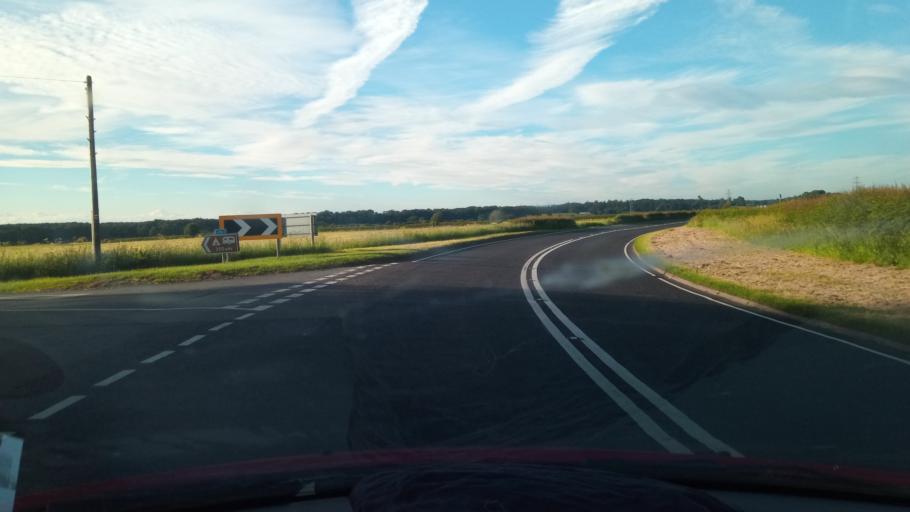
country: GB
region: Scotland
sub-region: Dumfries and Galloway
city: Gretna
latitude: 55.0198
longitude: -2.9854
